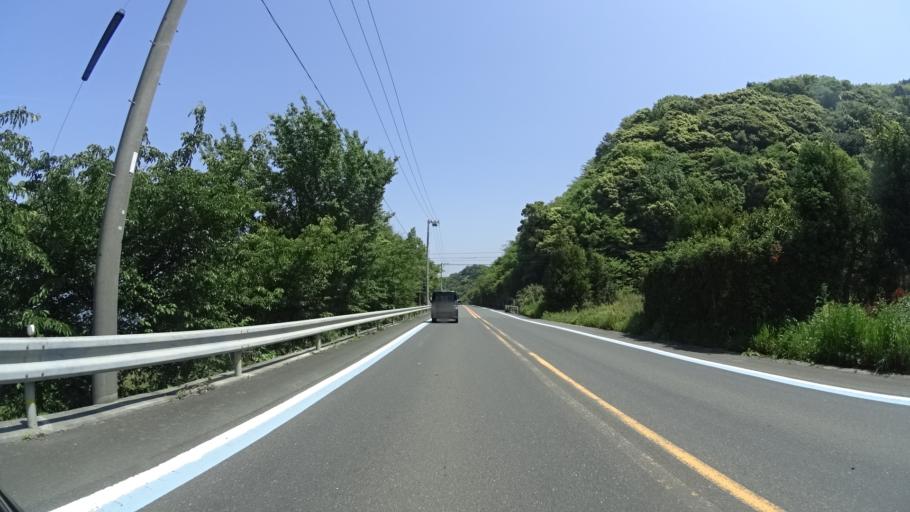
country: JP
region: Ehime
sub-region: Nishiuwa-gun
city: Ikata-cho
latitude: 33.5364
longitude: 132.4008
